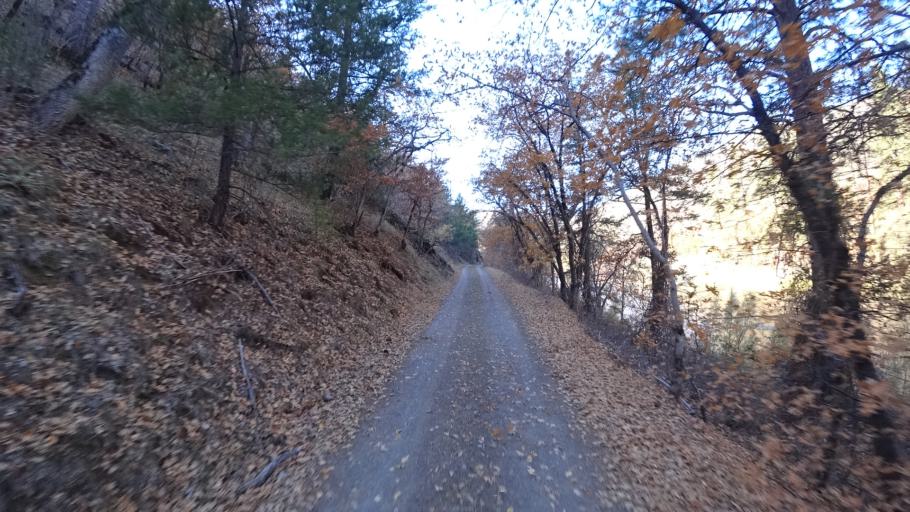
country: US
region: California
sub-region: Siskiyou County
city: Yreka
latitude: 41.8562
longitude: -122.7553
